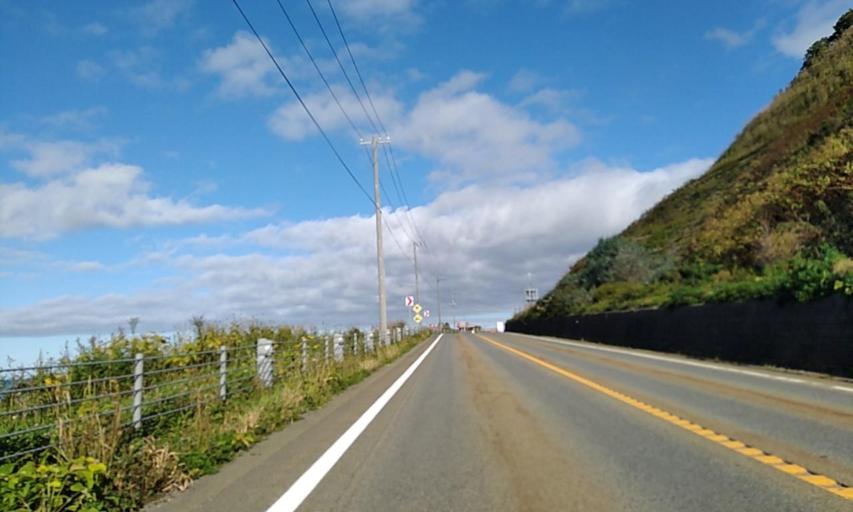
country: JP
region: Hokkaido
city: Shizunai-furukawacho
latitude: 42.2110
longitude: 142.6454
